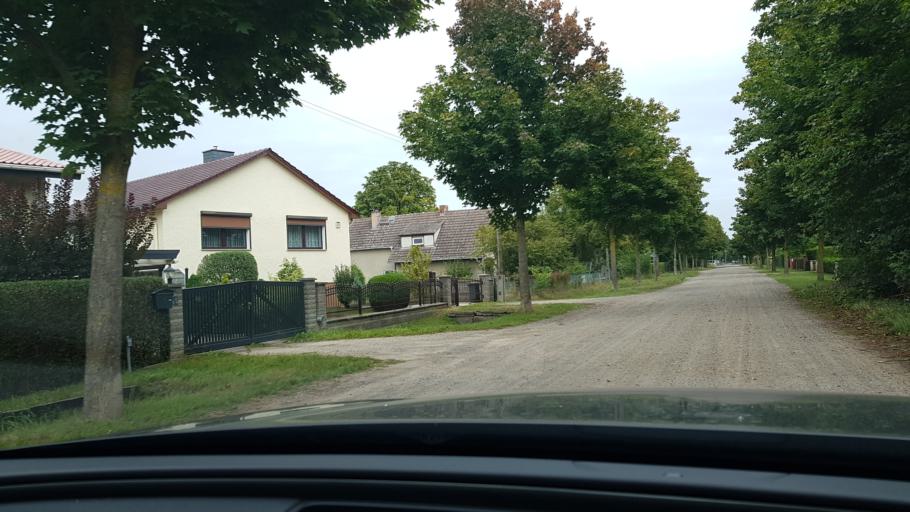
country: DE
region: Brandenburg
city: Brieselang
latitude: 52.5964
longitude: 12.9931
